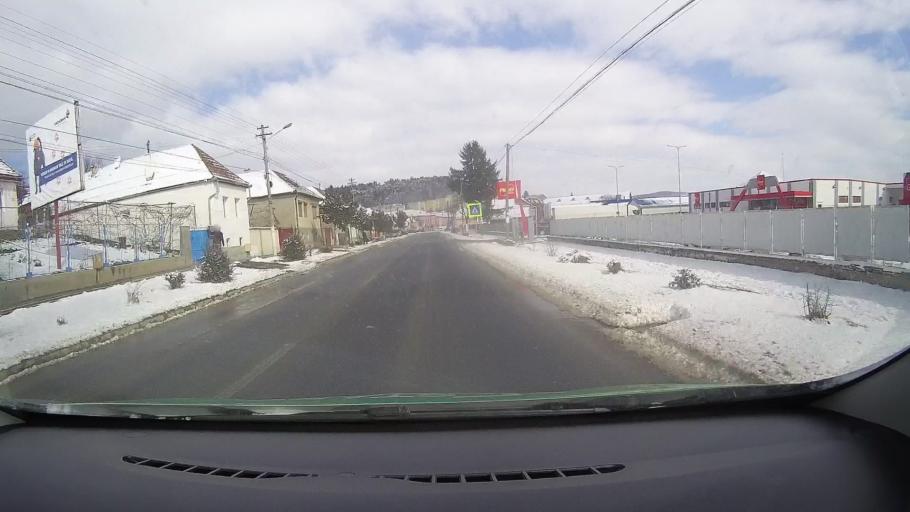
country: RO
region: Sibiu
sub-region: Oras Agnita
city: Agnita
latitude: 45.9747
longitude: 24.6116
